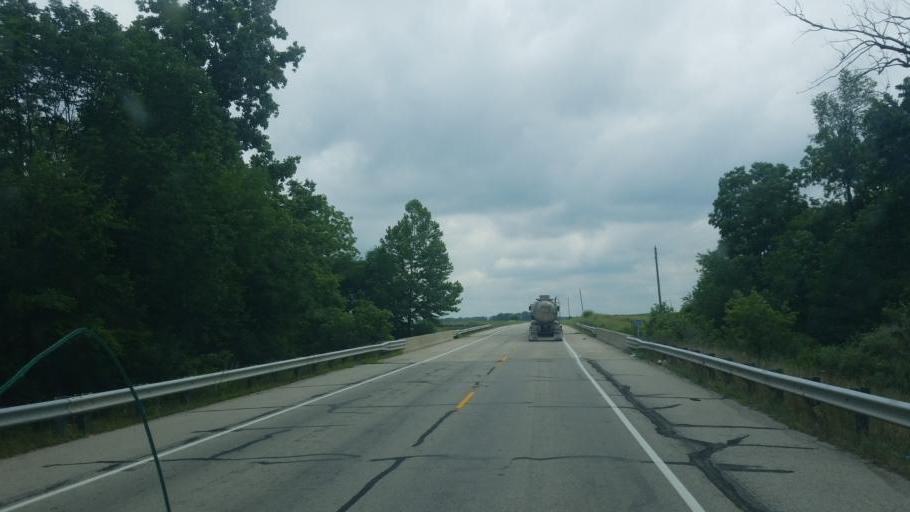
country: US
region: Indiana
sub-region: Huntington County
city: Warren
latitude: 40.6541
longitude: -85.3908
